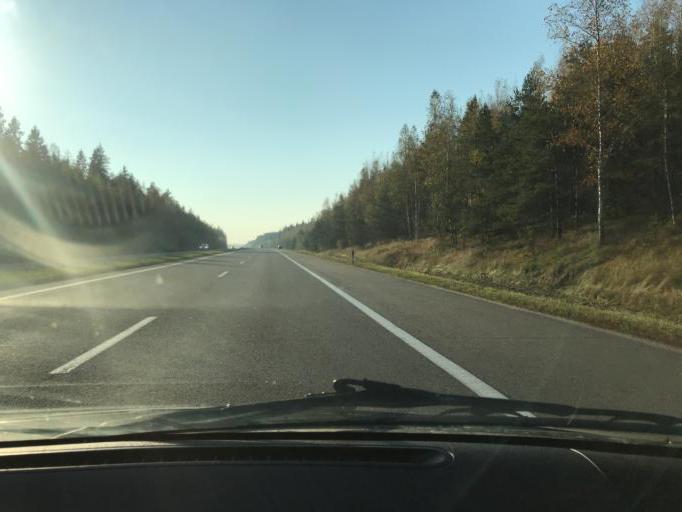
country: BY
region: Minsk
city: Krupki
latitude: 54.3096
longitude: 29.0143
